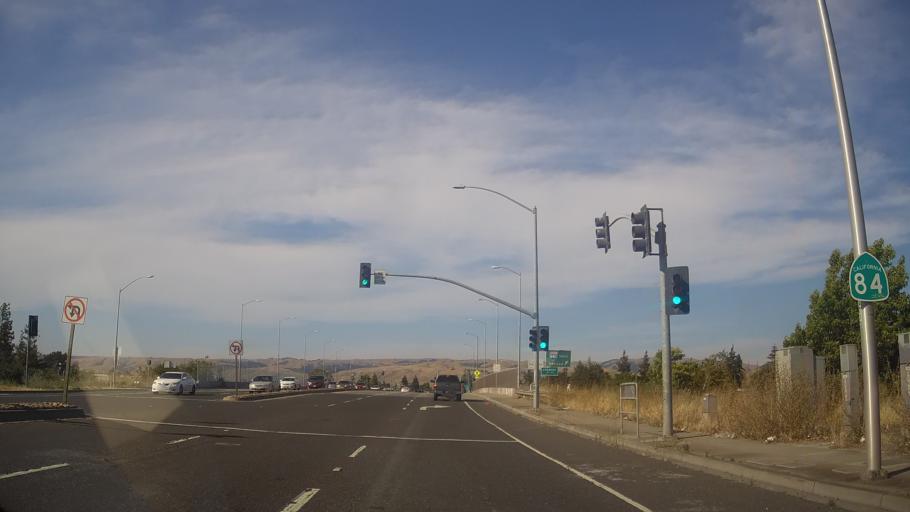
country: US
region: California
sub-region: Alameda County
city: Newark
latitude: 37.5457
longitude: -122.0238
